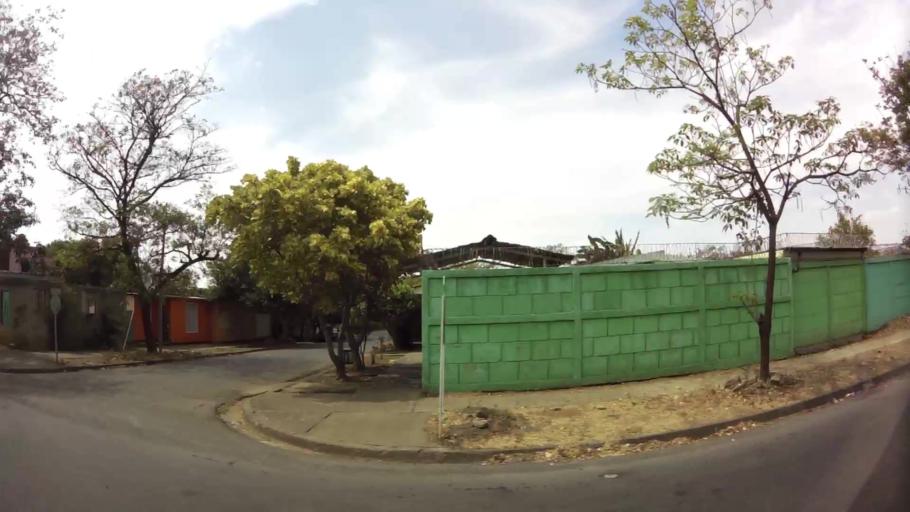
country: NI
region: Managua
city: Managua
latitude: 12.1508
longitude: -86.2798
